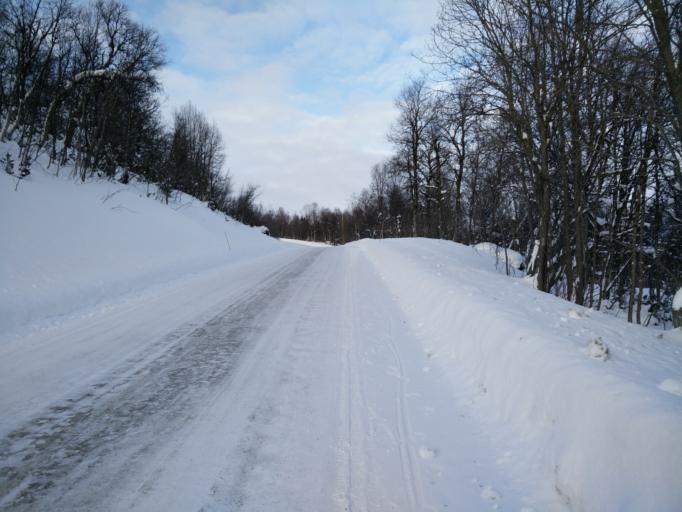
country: NO
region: Sor-Trondelag
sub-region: Tydal
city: Aas
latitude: 62.6494
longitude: 12.4123
